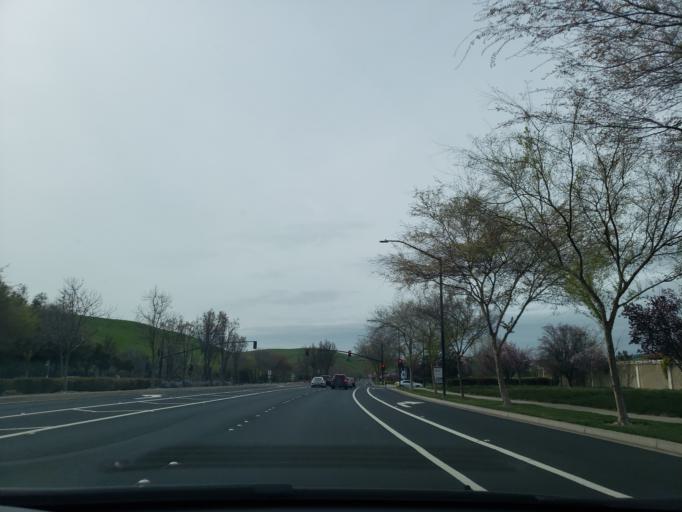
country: US
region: California
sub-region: Contra Costa County
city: Blackhawk
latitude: 37.7601
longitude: -121.9050
